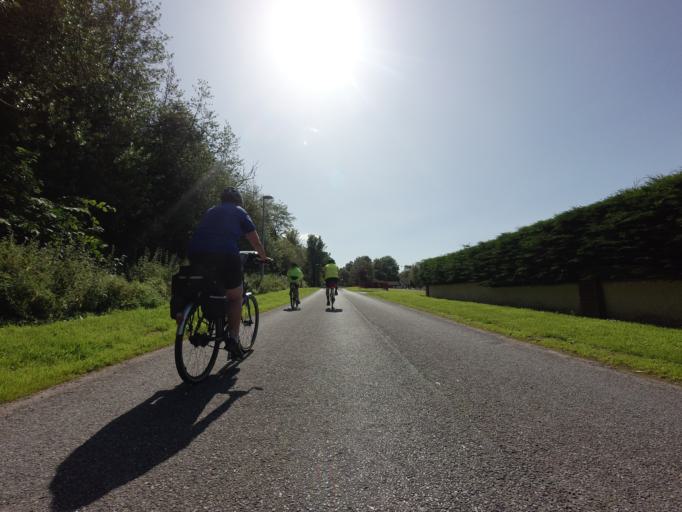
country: GB
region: Scotland
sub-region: Highland
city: Inverness
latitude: 57.4739
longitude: -4.1644
